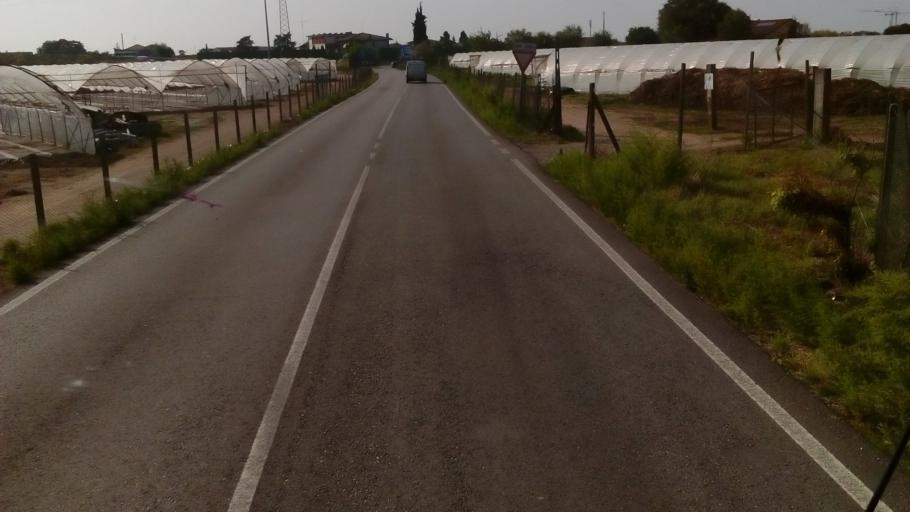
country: IT
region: Veneto
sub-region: Provincia di Verona
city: Campagnola
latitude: 45.3499
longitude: 11.0653
